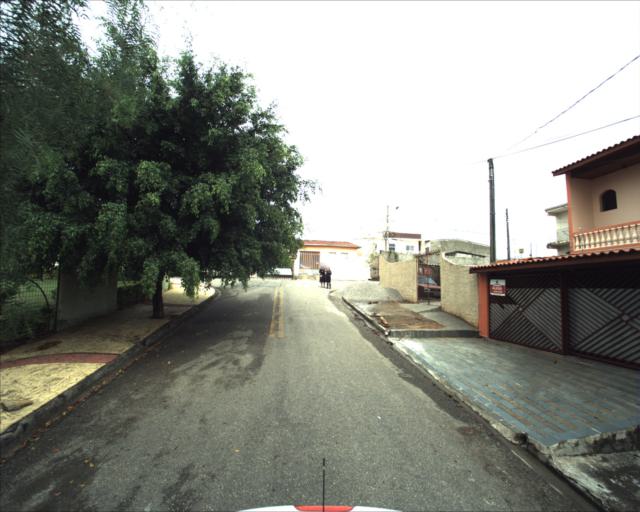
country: BR
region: Sao Paulo
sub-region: Sorocaba
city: Sorocaba
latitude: -23.5063
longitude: -47.5009
